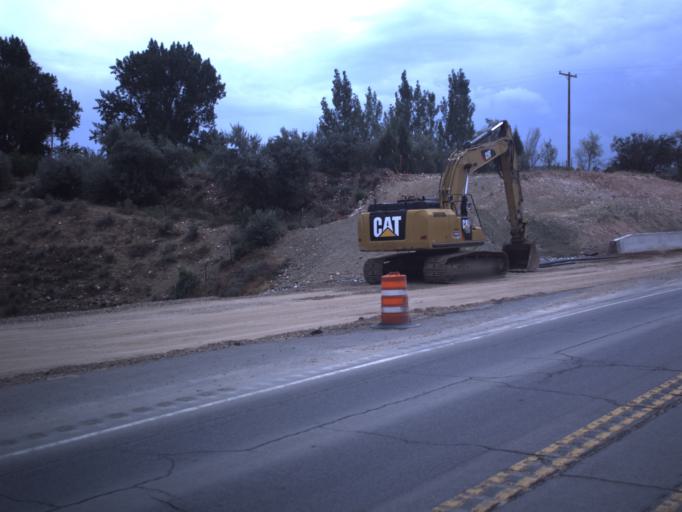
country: US
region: Utah
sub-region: Duchesne County
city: Roosevelt
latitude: 40.2493
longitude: -110.0675
